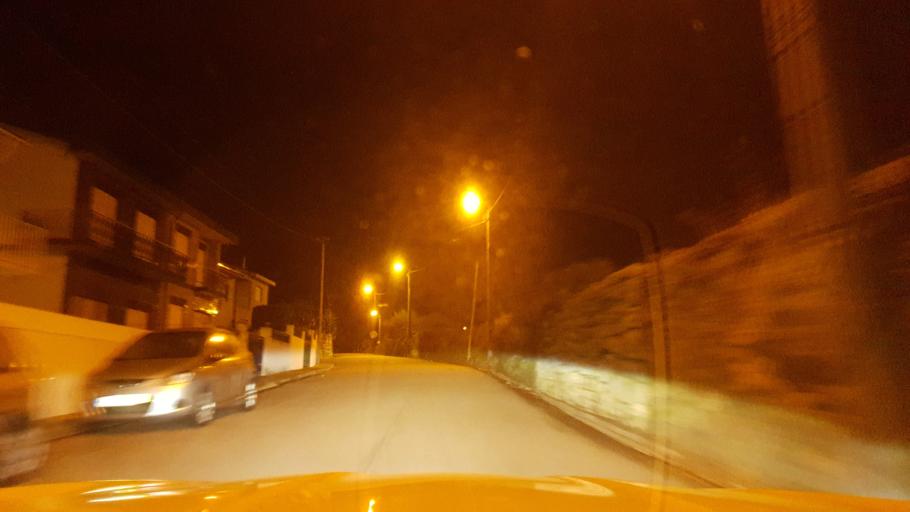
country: PT
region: Porto
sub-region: Matosinhos
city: Guifoes
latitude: 41.2148
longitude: -8.6445
